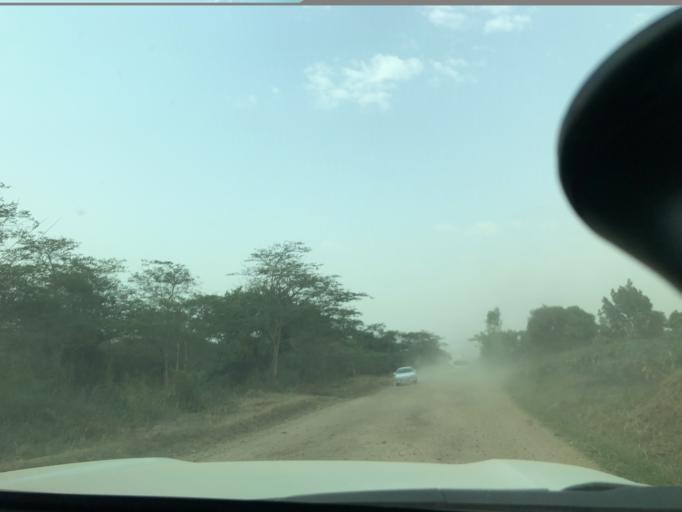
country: CD
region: Nord Kivu
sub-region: North Kivu
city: Butembo
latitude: 0.1520
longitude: 29.6407
